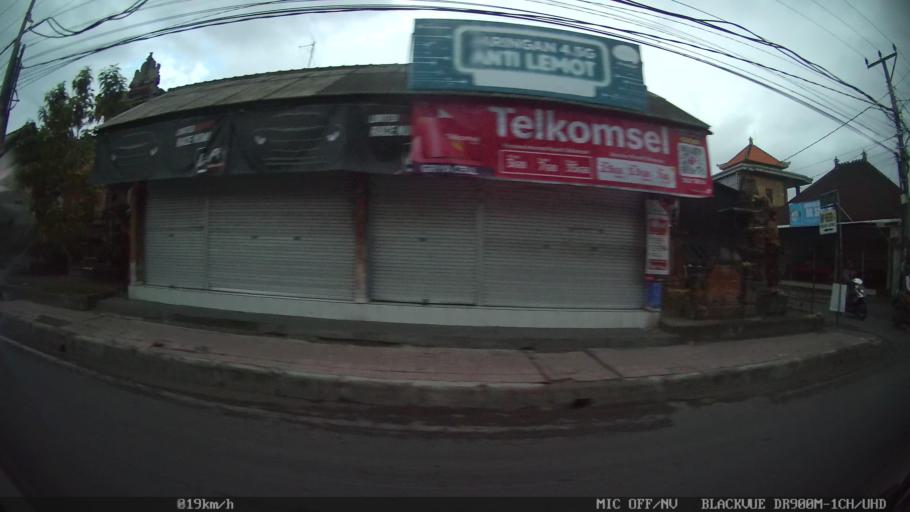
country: ID
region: Bali
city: Banjar Pasekan
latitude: -8.6275
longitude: 115.2843
